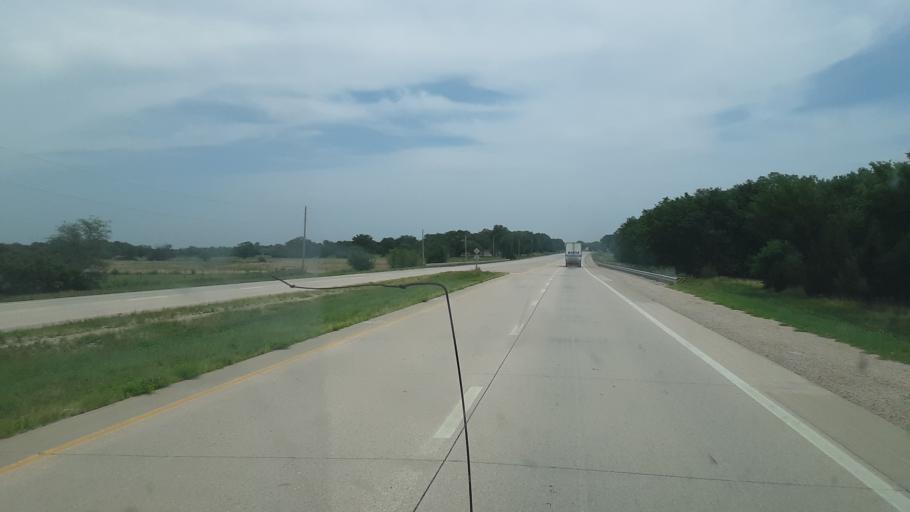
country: US
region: Kansas
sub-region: Allen County
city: Iola
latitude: 37.9220
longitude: -95.3164
